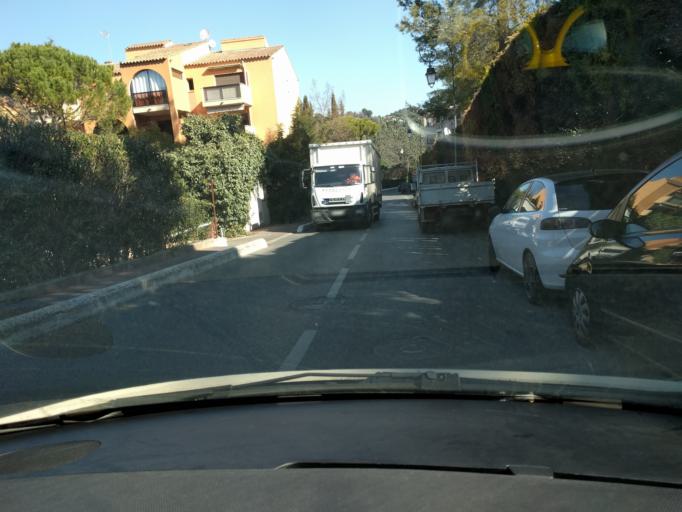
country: FR
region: Provence-Alpes-Cote d'Azur
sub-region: Departement des Alpes-Maritimes
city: Mougins
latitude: 43.6017
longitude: 6.9880
